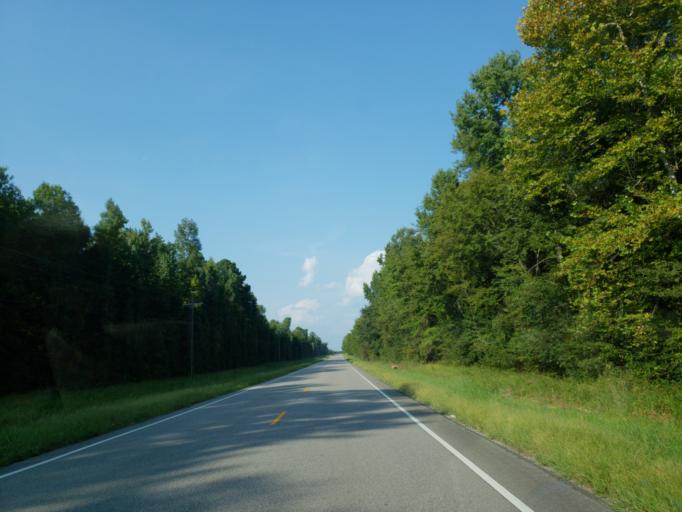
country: US
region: Alabama
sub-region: Greene County
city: Eutaw
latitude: 32.7378
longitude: -88.0536
